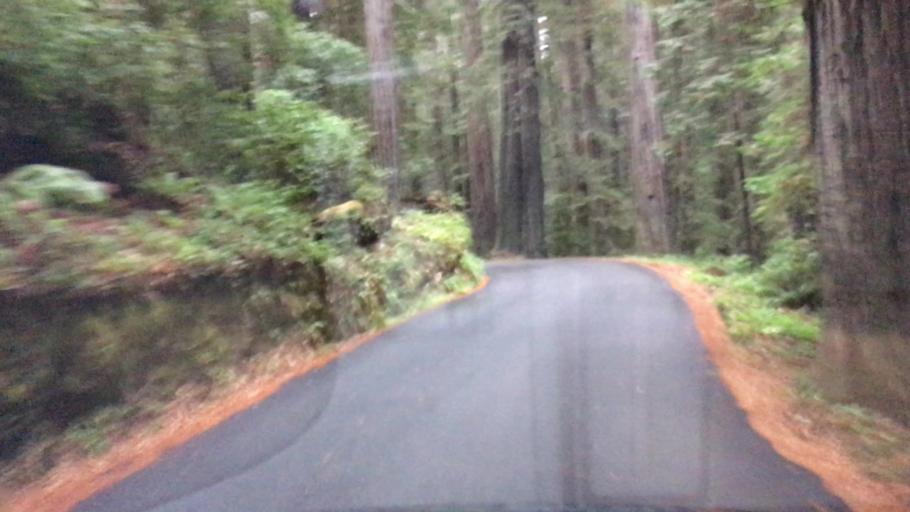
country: US
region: California
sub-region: Humboldt County
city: Rio Dell
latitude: 40.3529
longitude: -123.9755
